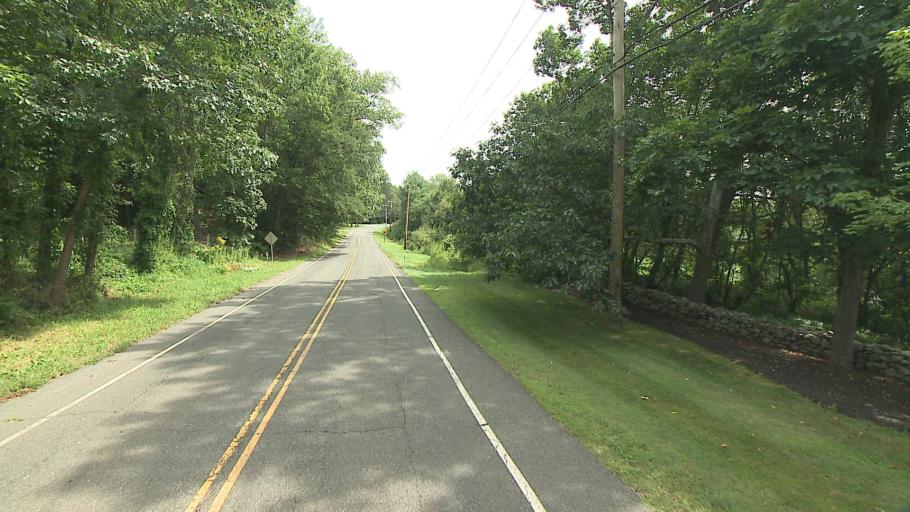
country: US
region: Connecticut
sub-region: Litchfield County
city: Bethlehem Village
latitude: 41.5942
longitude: -73.2364
